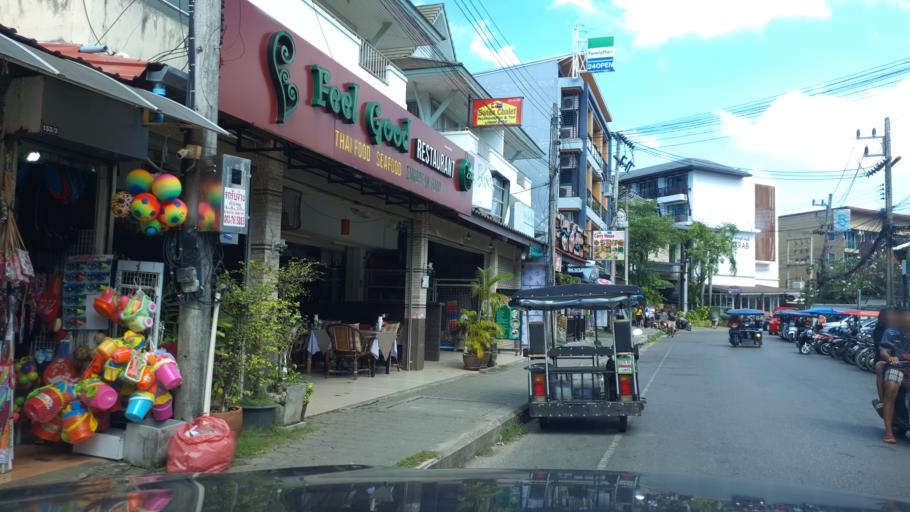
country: TH
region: Phangnga
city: Ban Ao Nang
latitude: 8.0400
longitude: 98.8175
